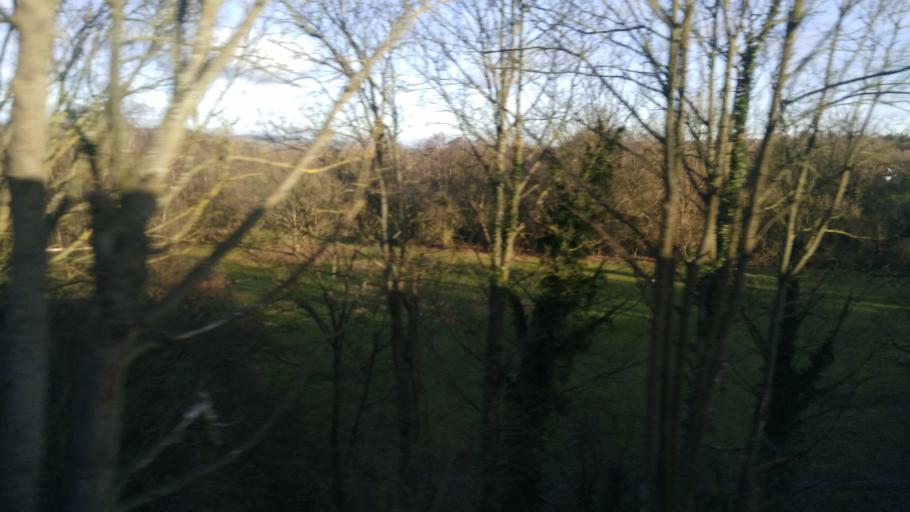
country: GB
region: England
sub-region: Kent
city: Sevenoaks
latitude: 51.2875
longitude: 0.1703
